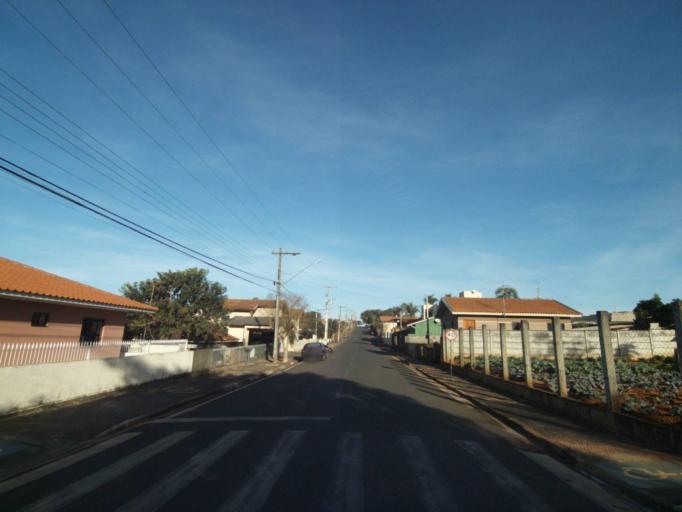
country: BR
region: Parana
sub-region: Tibagi
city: Tibagi
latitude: -24.5185
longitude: -50.4072
